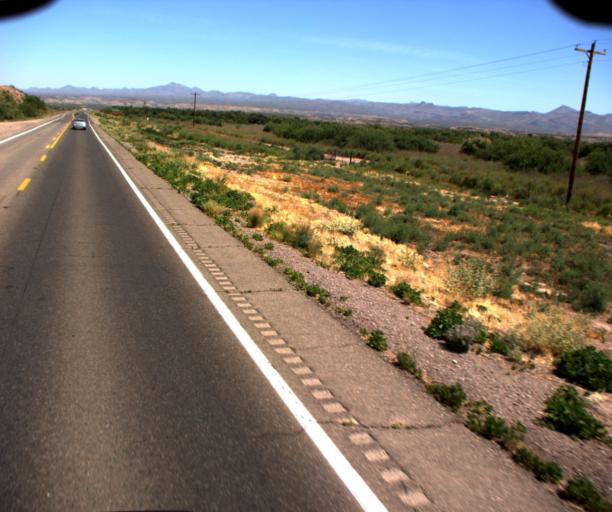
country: US
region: Arizona
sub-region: Graham County
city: Bylas
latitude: 33.1515
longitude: -110.1276
